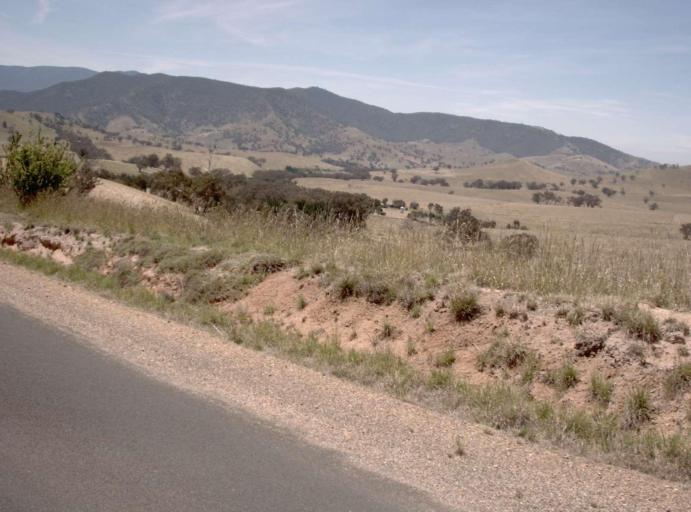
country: AU
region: Victoria
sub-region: East Gippsland
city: Bairnsdale
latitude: -37.1672
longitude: 147.6805
